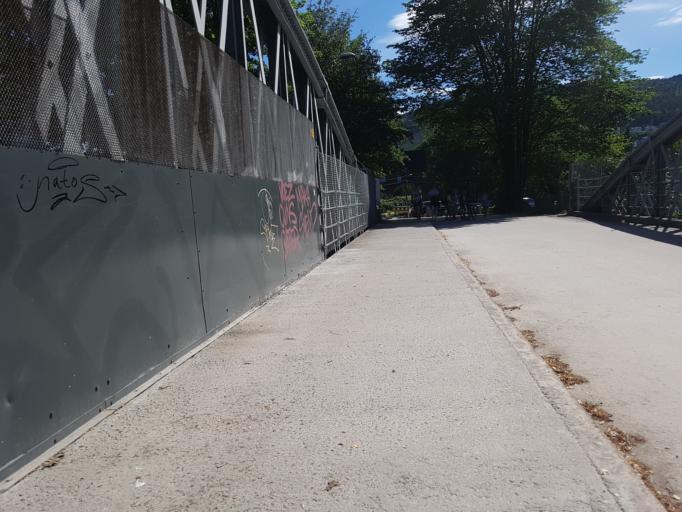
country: NO
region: Buskerud
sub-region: Drammen
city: Drammen
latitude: 59.7423
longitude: 10.1867
